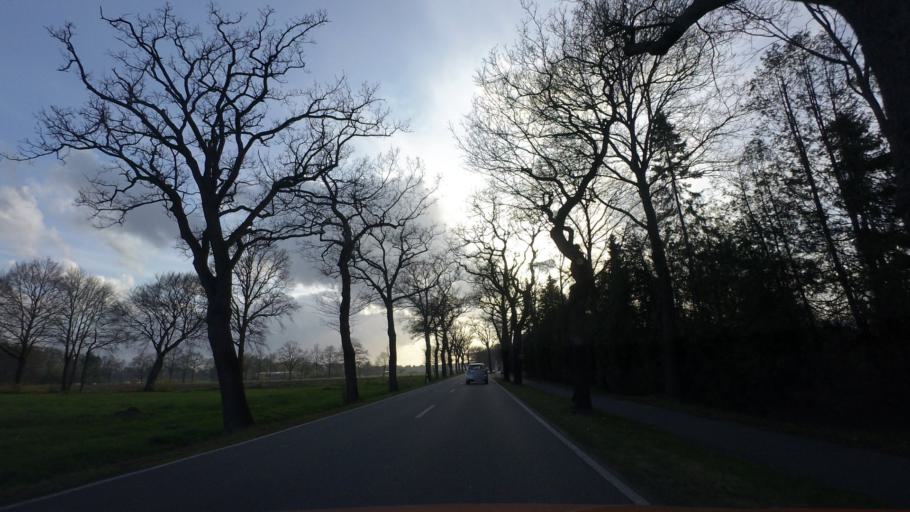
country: DE
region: Lower Saxony
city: Oldenburg
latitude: 53.1258
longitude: 8.1584
